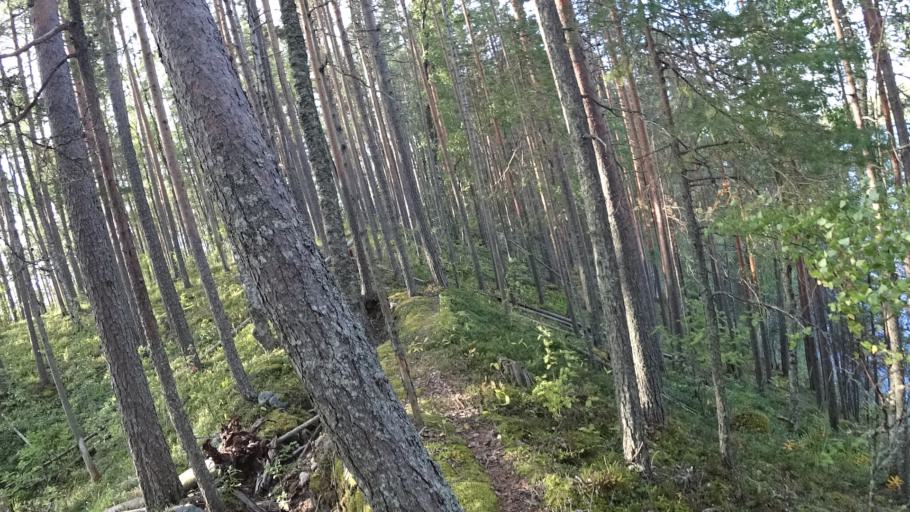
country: FI
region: North Karelia
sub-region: Joensuu
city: Ilomantsi
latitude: 62.5716
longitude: 31.1774
